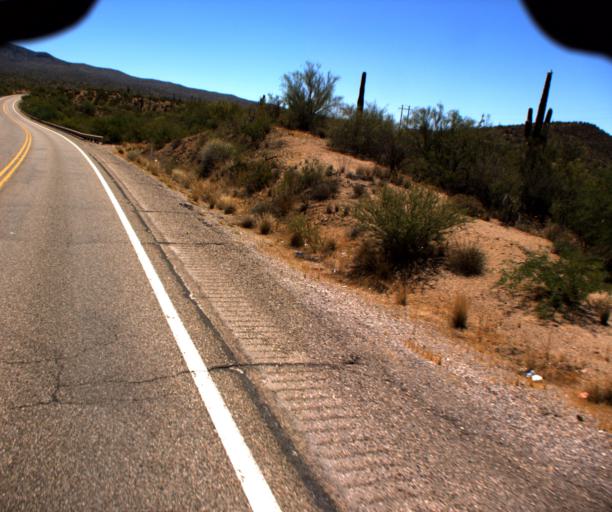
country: US
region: Arizona
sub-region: Pinal County
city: Kearny
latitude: 33.1172
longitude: -110.9685
